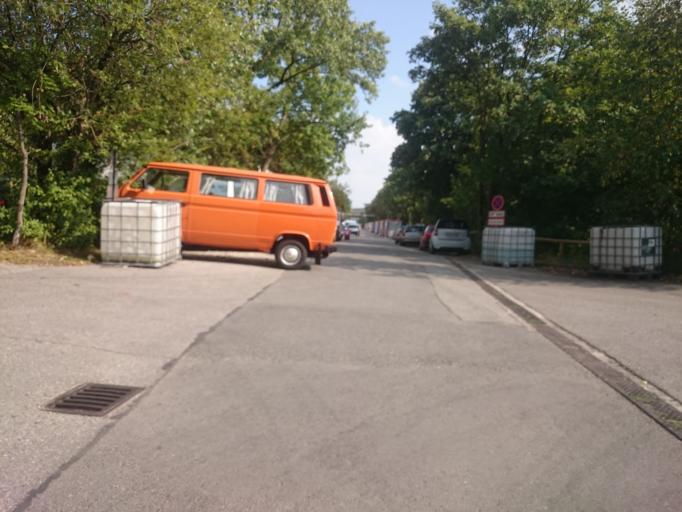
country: DE
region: Bavaria
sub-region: Upper Bavaria
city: Munich
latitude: 48.1574
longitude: 11.5537
